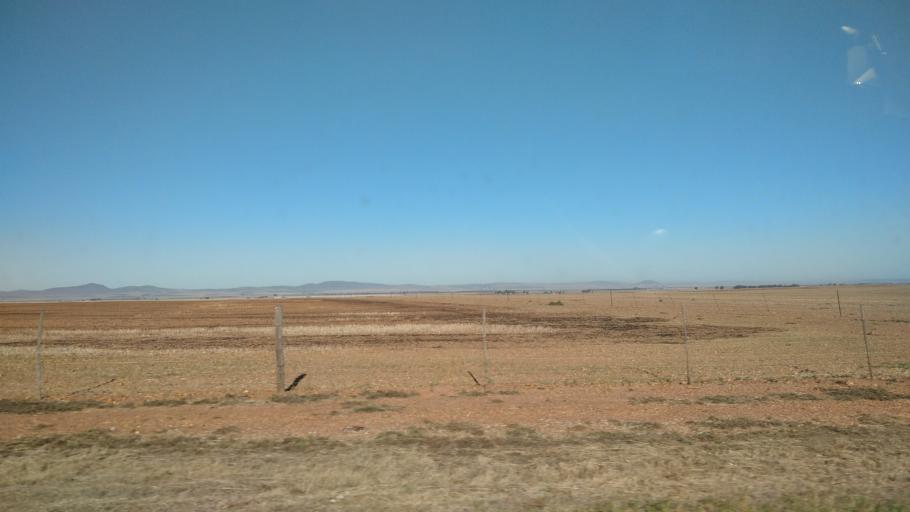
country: ZA
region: Western Cape
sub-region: West Coast District Municipality
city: Moorreesburg
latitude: -33.3152
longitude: 18.6225
